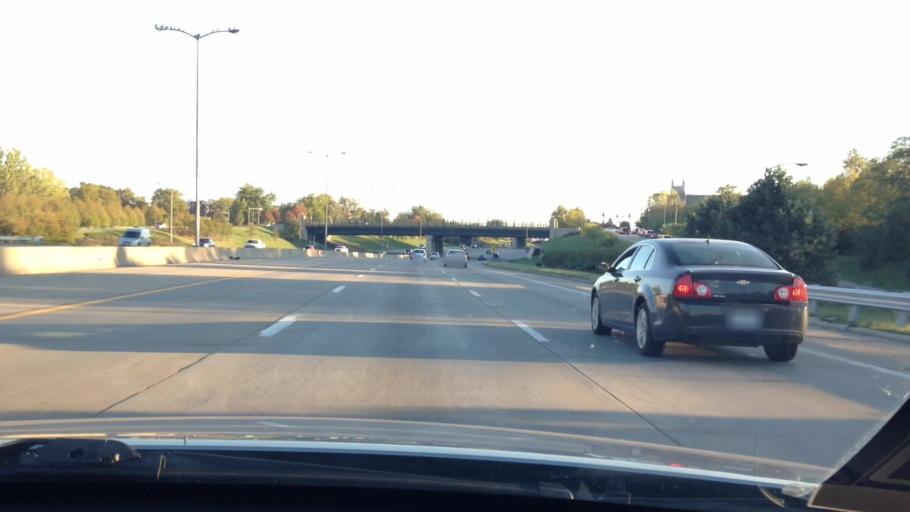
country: US
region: Missouri
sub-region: Jackson County
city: Kansas City
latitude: 39.0727
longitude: -94.5611
